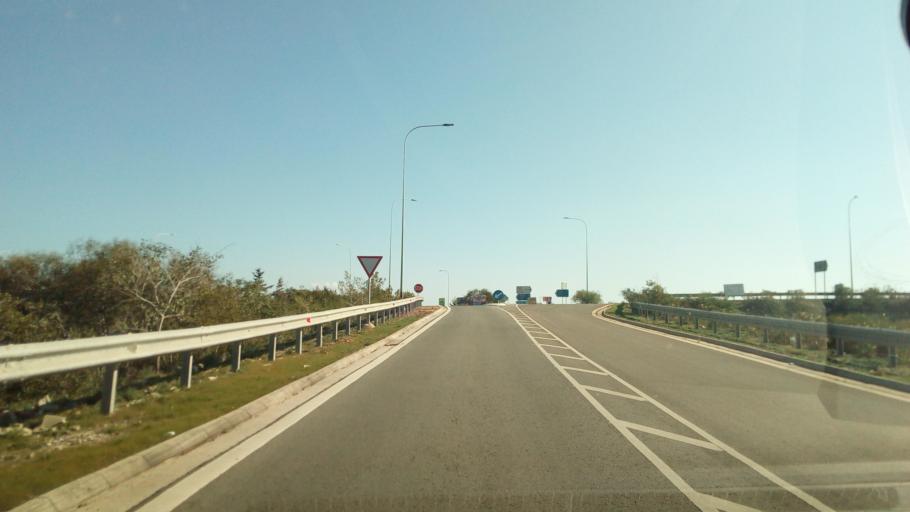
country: CY
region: Ammochostos
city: Avgorou
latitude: 34.9732
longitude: 33.8289
